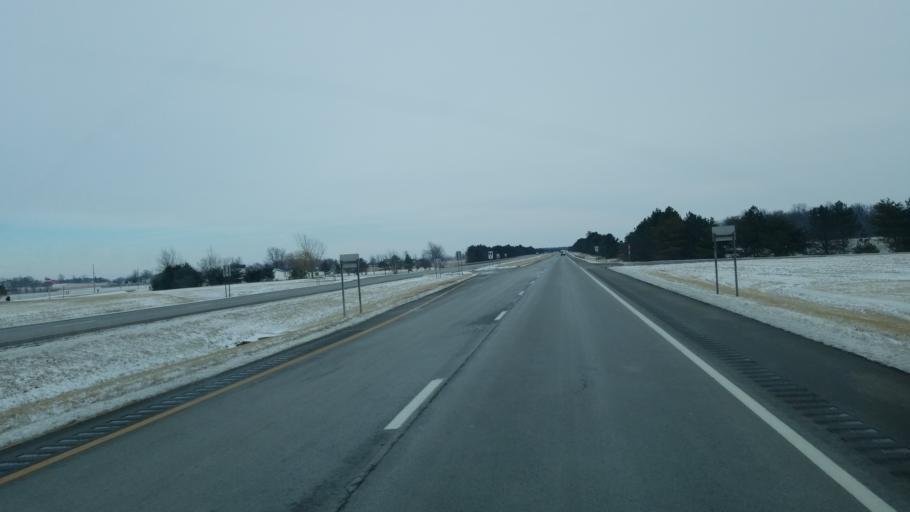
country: US
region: Ohio
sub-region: Wyandot County
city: Carey
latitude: 40.9572
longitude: -83.4482
